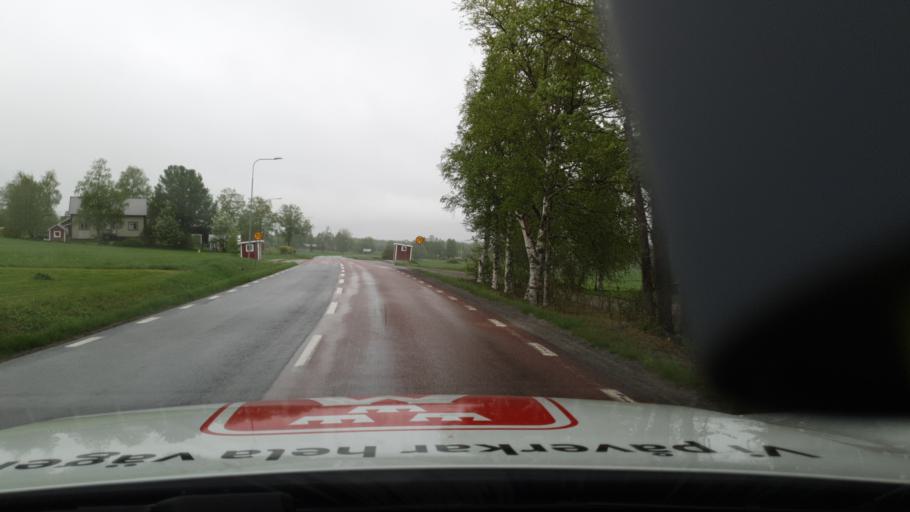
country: SE
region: Jaemtland
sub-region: Stroemsunds Kommun
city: Stroemsund
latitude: 63.8180
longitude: 15.5186
